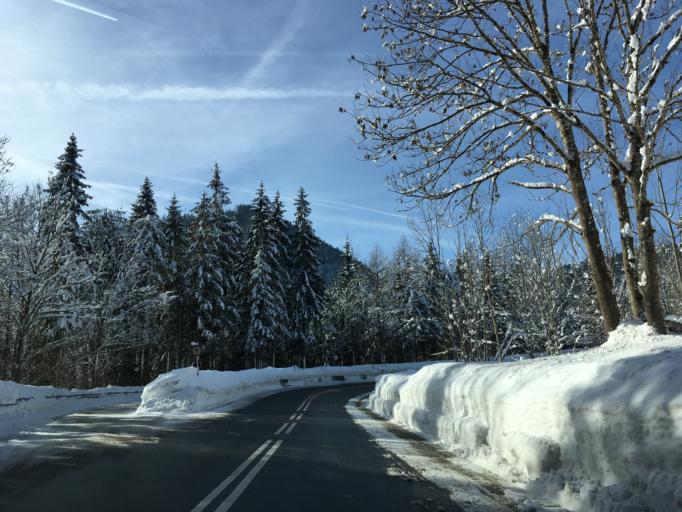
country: DE
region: Bavaria
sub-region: Upper Bavaria
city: Burg Unter-Falkenstein
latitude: 47.6704
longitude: 12.0750
